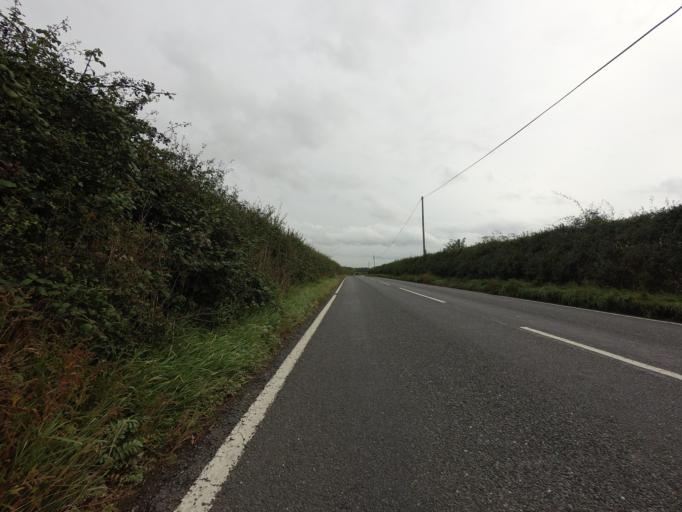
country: GB
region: England
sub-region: Cambridgeshire
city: Duxford
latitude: 52.0198
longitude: 0.1429
